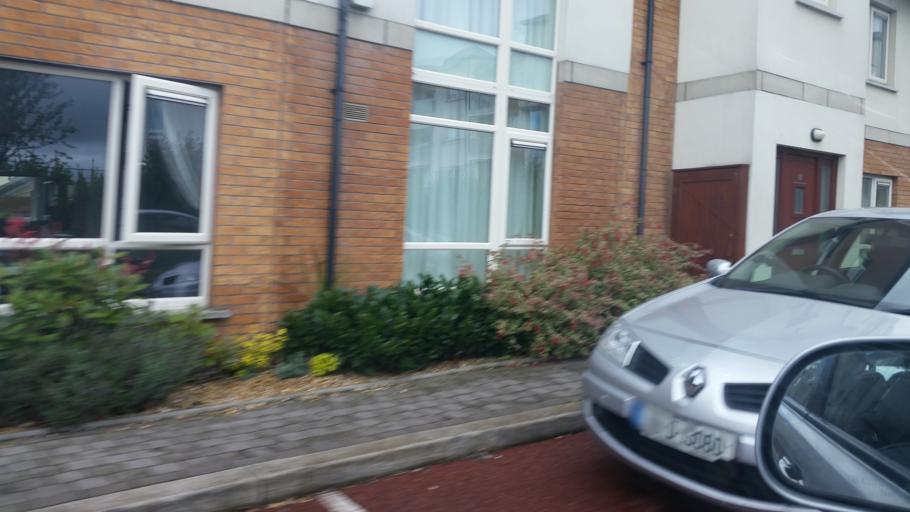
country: IE
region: Leinster
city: Donaghmede
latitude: 53.4042
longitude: -6.1741
